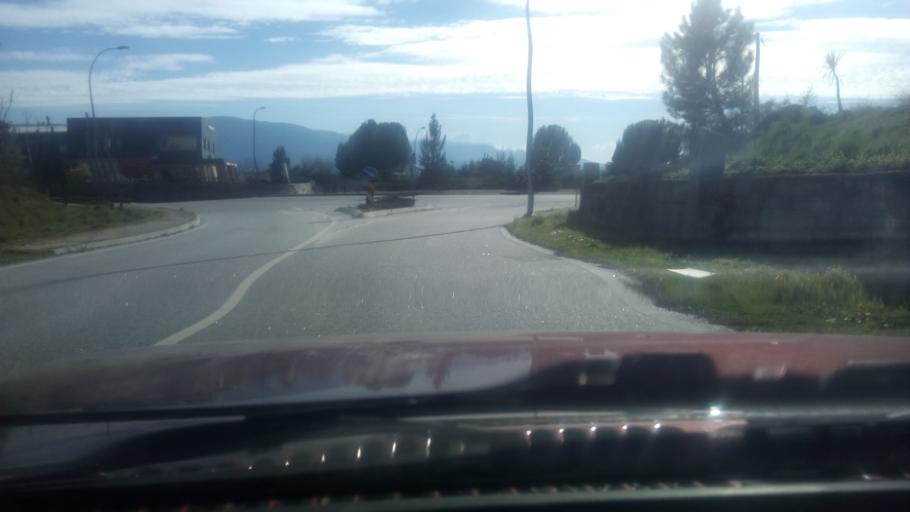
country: PT
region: Guarda
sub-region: Fornos de Algodres
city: Fornos de Algodres
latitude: 40.6150
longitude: -7.5327
